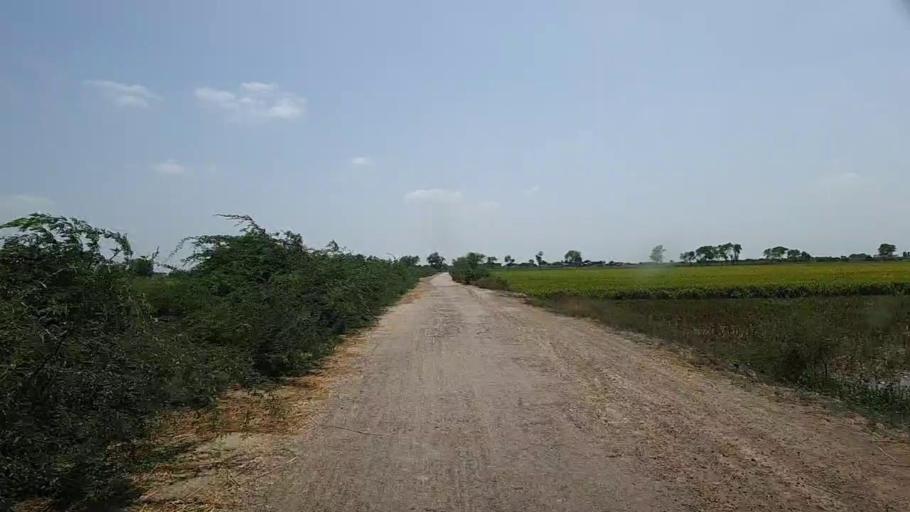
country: PK
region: Sindh
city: Kario
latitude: 24.6458
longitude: 68.5640
